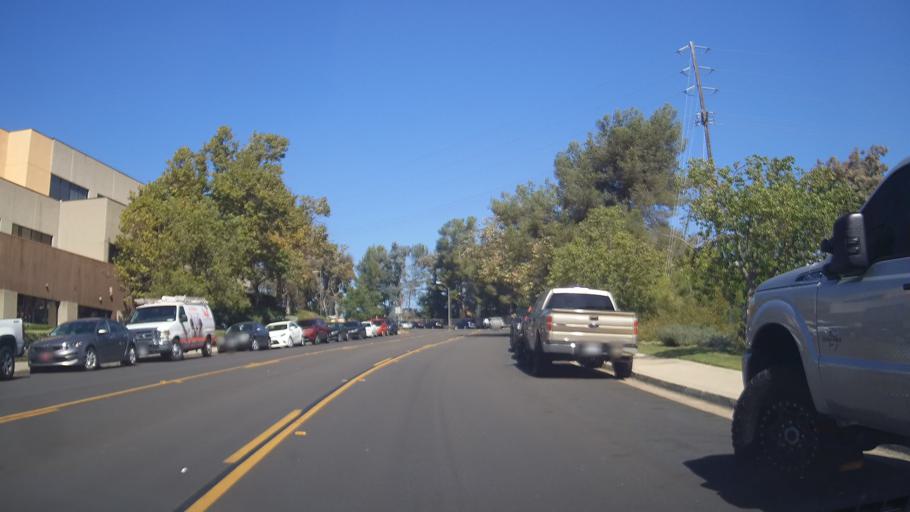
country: US
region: California
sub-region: San Diego County
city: La Mesa
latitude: 32.8273
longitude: -117.1215
